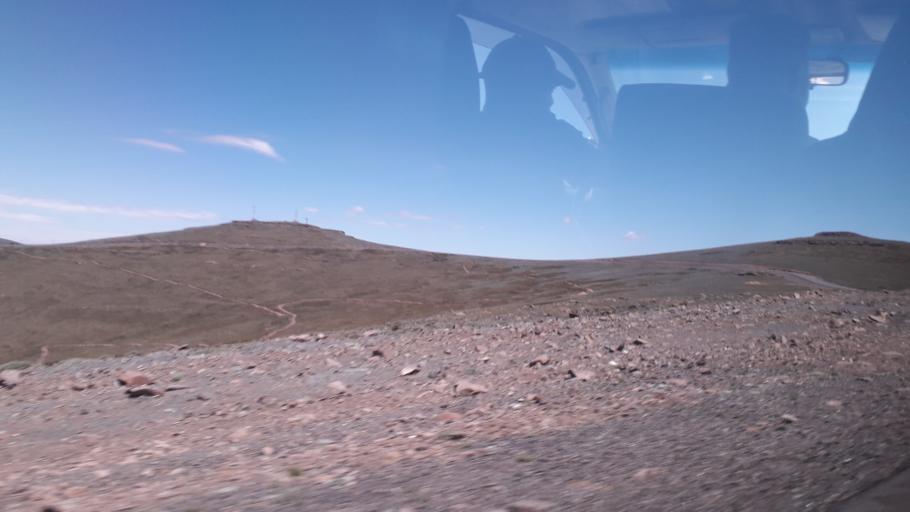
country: ZA
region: Orange Free State
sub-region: Thabo Mofutsanyana District Municipality
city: Phuthaditjhaba
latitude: -28.8149
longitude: 28.7359
